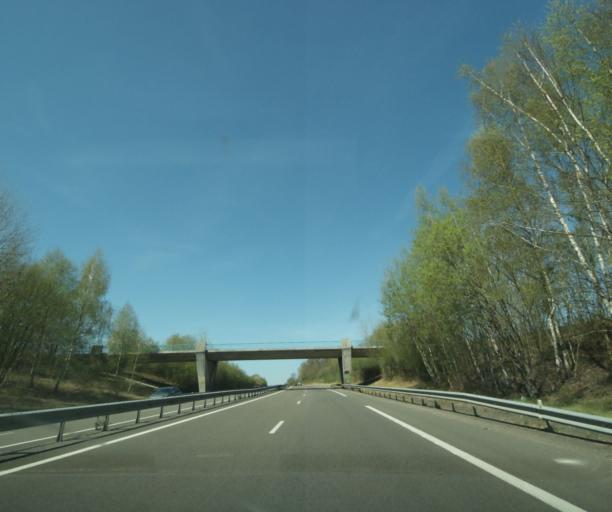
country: FR
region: Bourgogne
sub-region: Departement de la Nievre
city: Coulanges-les-Nevers
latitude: 47.0190
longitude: 3.1958
